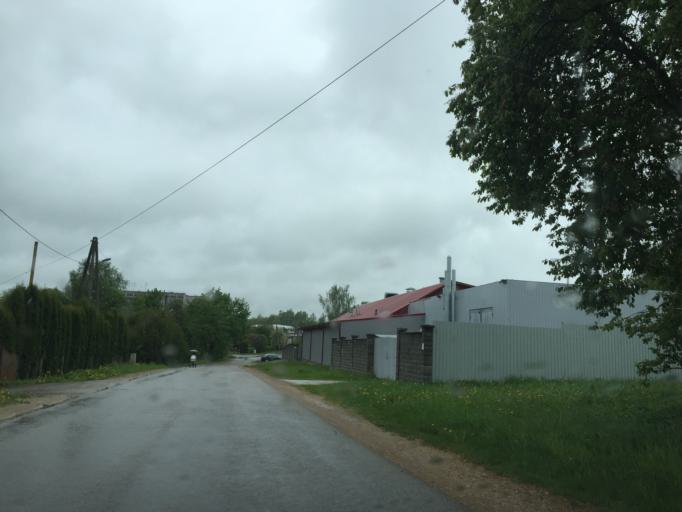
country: LV
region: Lielvarde
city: Lielvarde
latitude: 56.7212
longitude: 24.7969
